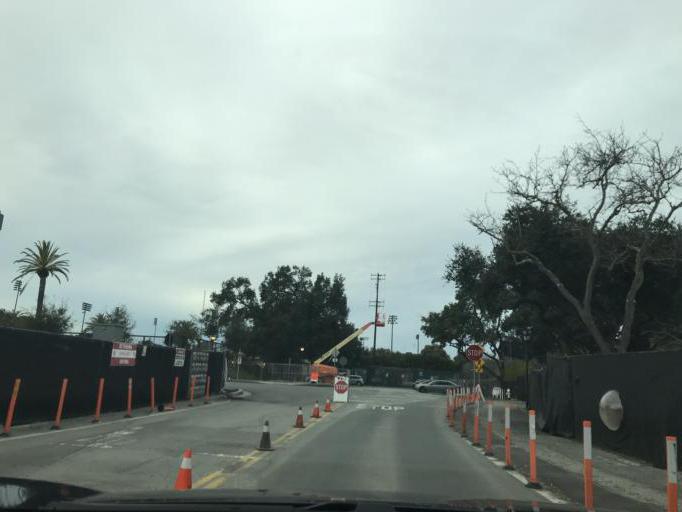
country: US
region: California
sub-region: Santa Clara County
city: Stanford
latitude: 37.4298
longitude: -122.1561
